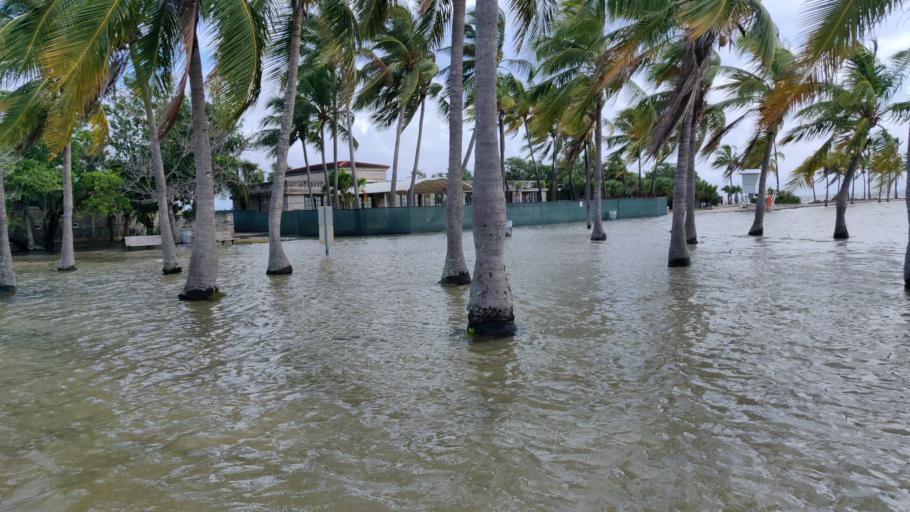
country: US
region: Florida
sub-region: Miami-Dade County
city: Coconut Grove
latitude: 25.6787
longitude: -80.2571
